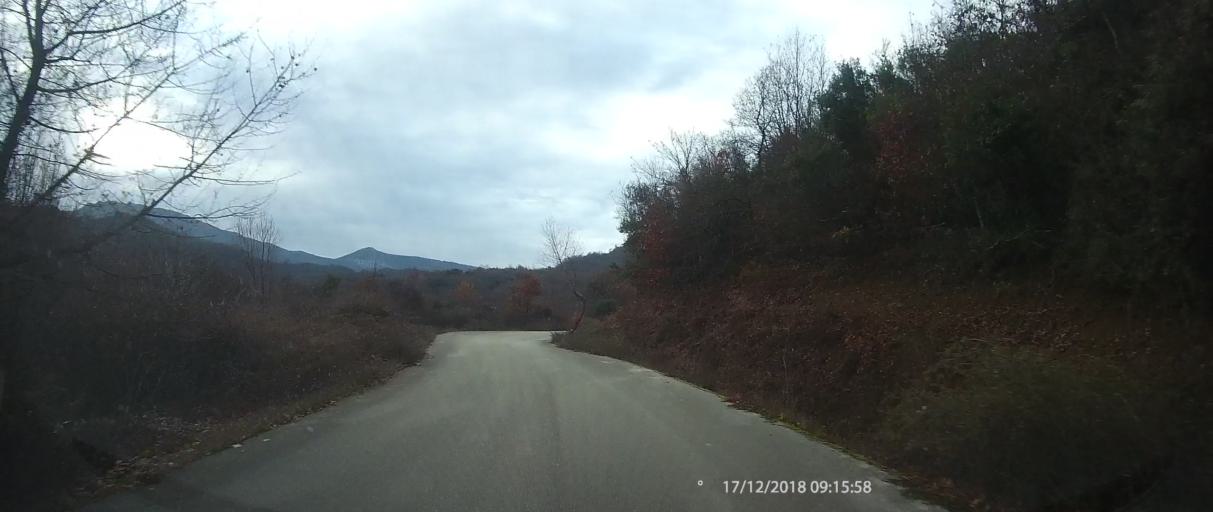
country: GR
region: Epirus
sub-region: Nomos Ioanninon
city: Kalpaki
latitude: 39.9643
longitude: 20.6568
